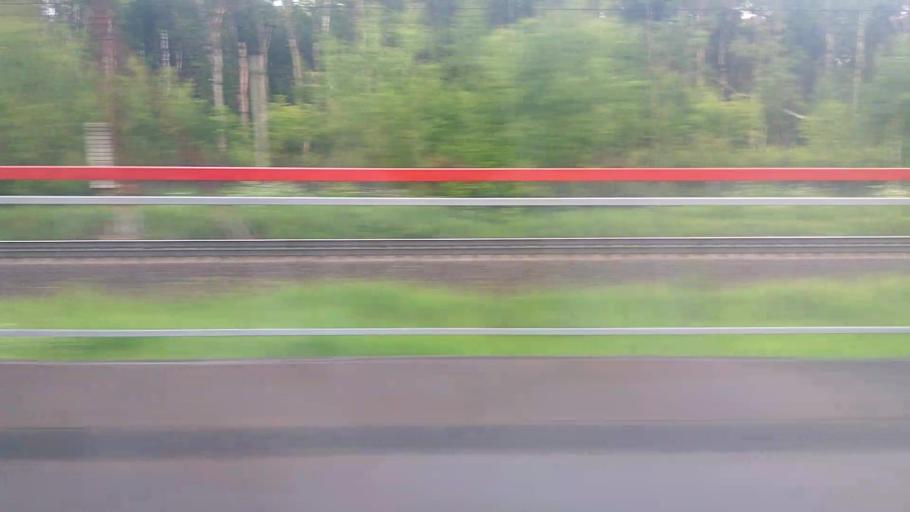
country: RU
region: Moskovskaya
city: Zhilevo
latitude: 55.0610
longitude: 37.9894
